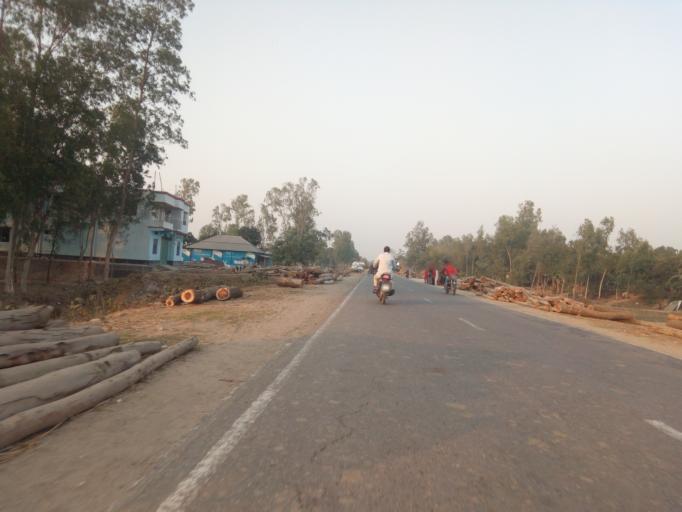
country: BD
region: Rajshahi
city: Bogra
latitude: 24.5947
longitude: 89.2372
